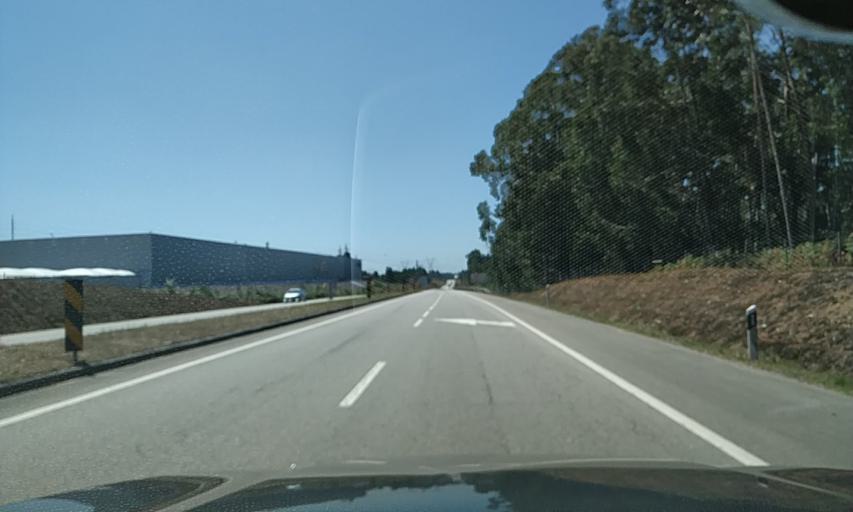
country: PT
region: Aveiro
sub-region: Agueda
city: Agueda
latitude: 40.5908
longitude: -8.4703
